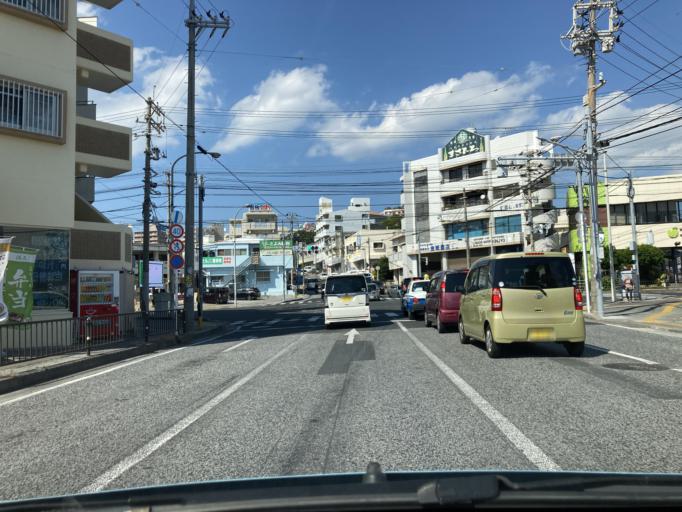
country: JP
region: Okinawa
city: Tomigusuku
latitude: 26.1957
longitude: 127.7050
